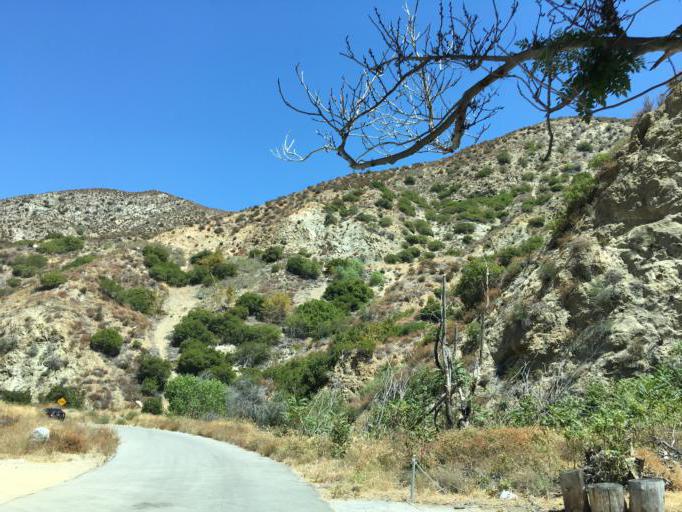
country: US
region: California
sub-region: Los Angeles County
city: La Crescenta-Montrose
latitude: 34.2919
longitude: -118.2345
